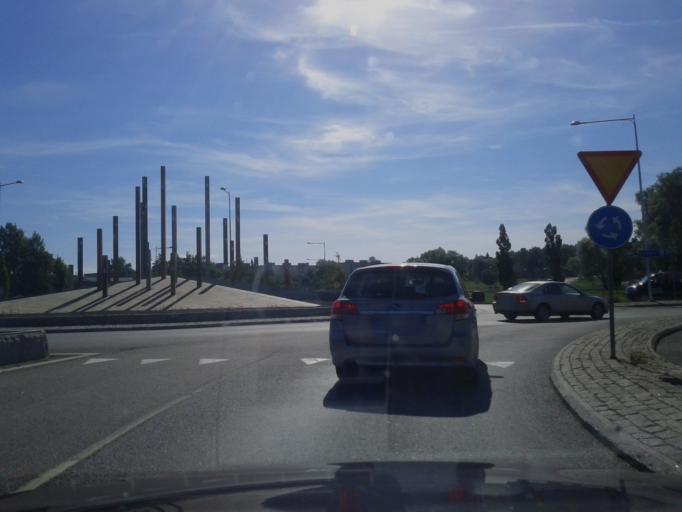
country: SE
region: Stockholm
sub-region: Taby Kommun
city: Taby
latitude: 59.4491
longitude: 18.0902
